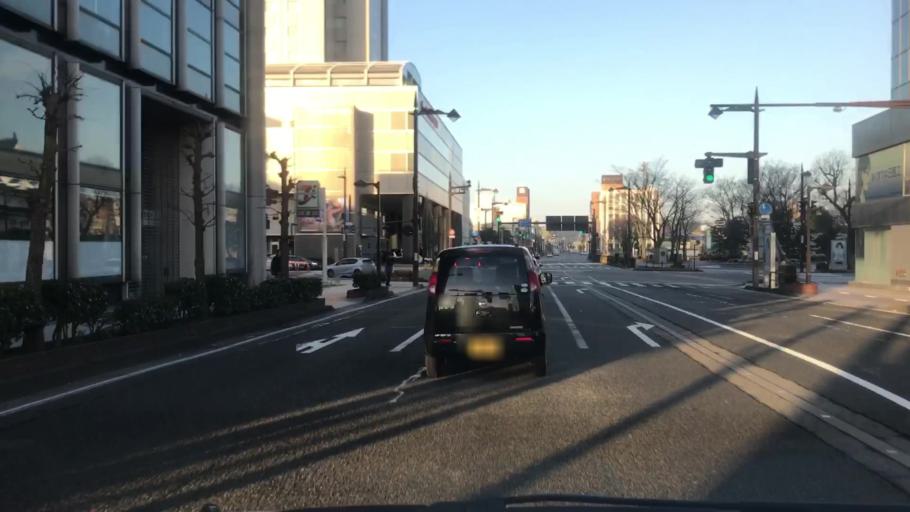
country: JP
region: Toyama
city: Toyama-shi
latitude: 36.6919
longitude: 137.2133
